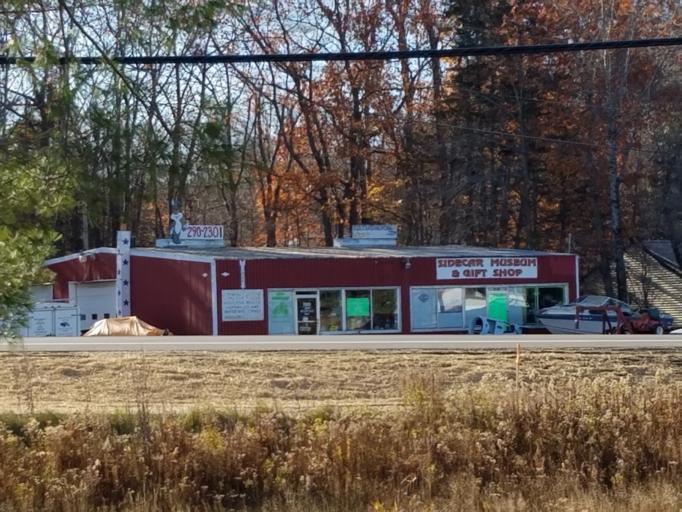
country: US
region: Maine
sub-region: Penobscot County
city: Howland
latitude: 45.2364
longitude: -68.6558
